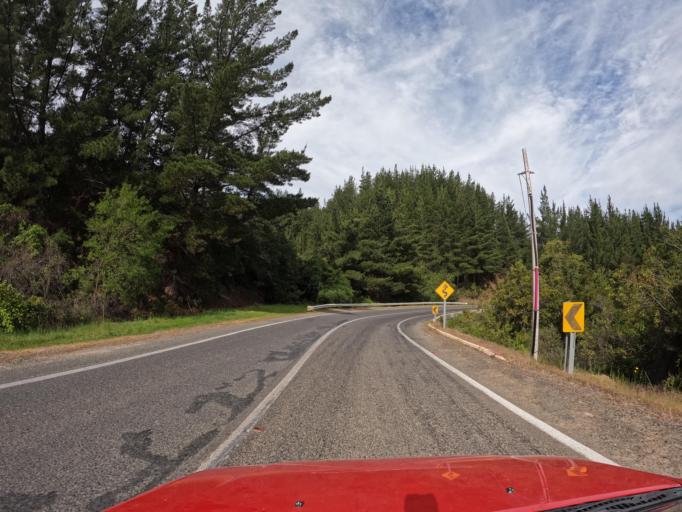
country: CL
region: Maule
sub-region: Provincia de Talca
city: Talca
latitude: -35.2961
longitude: -71.9710
